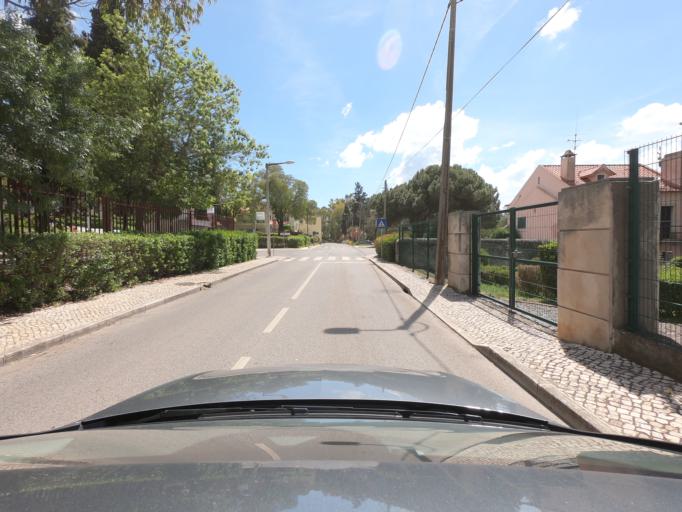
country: PT
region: Lisbon
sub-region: Oeiras
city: Linda-a-Velha
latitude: 38.7056
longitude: -9.2524
